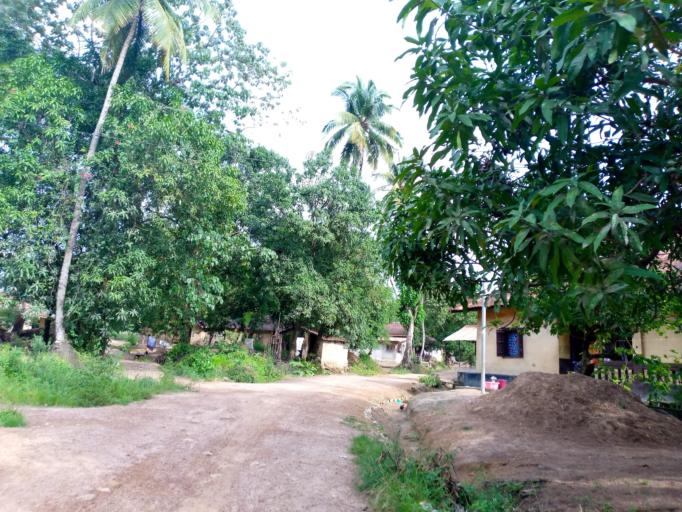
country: SL
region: Northern Province
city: Magburaka
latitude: 8.7190
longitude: -11.9509
